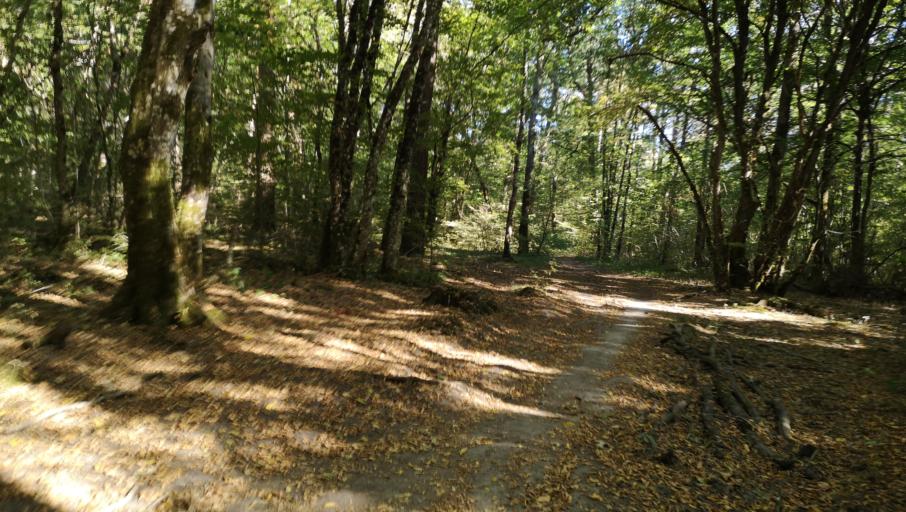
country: FR
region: Centre
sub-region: Departement du Loiret
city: Saran
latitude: 47.9597
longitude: 1.9009
